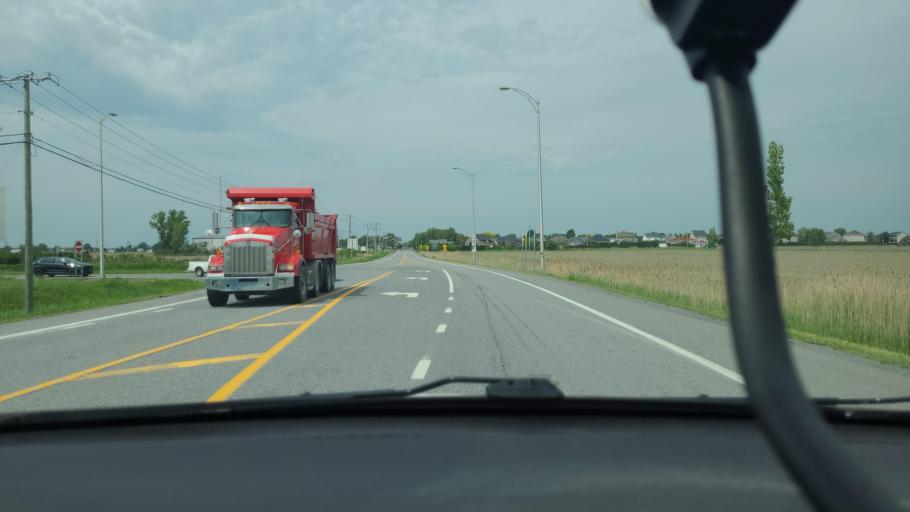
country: CA
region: Quebec
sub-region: Monteregie
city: Saint-Hyacinthe
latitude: 45.6354
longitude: -72.9958
